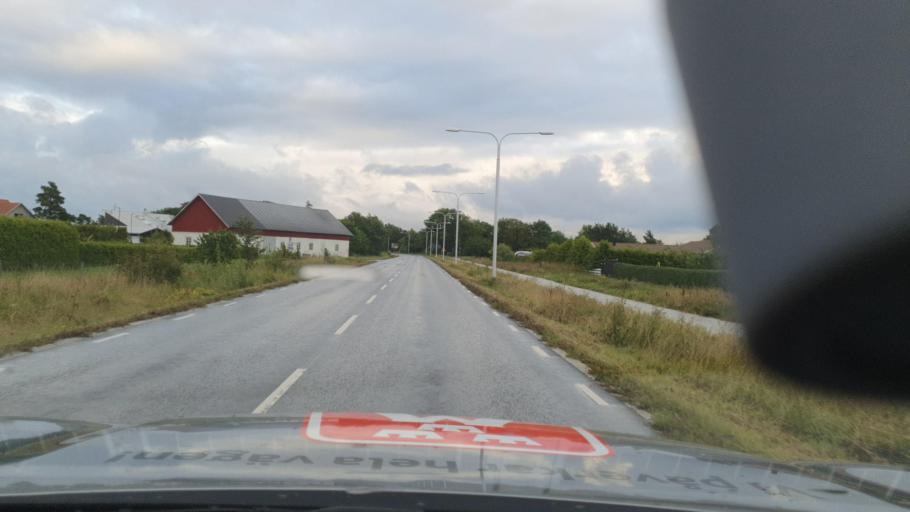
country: SE
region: Gotland
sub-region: Gotland
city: Vibble
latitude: 57.6060
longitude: 18.2377
